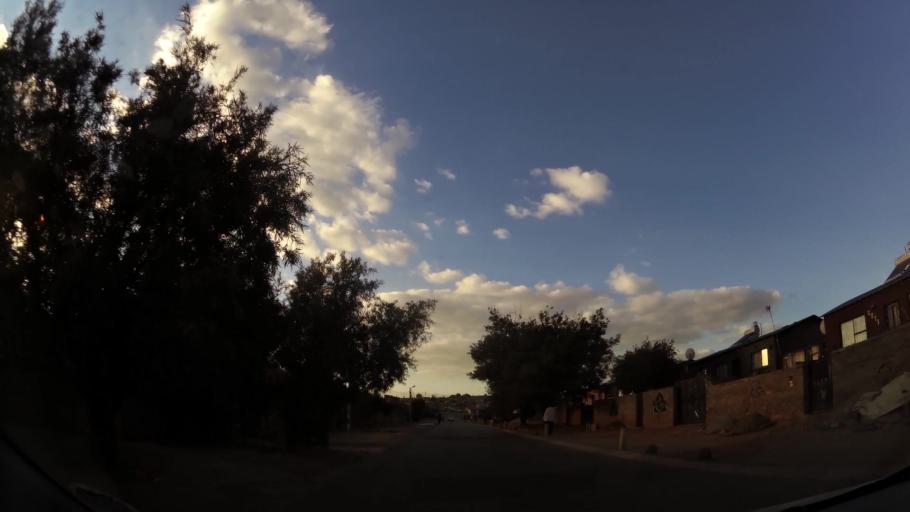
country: ZA
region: Gauteng
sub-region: West Rand District Municipality
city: Krugersdorp
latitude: -26.0787
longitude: 27.7476
